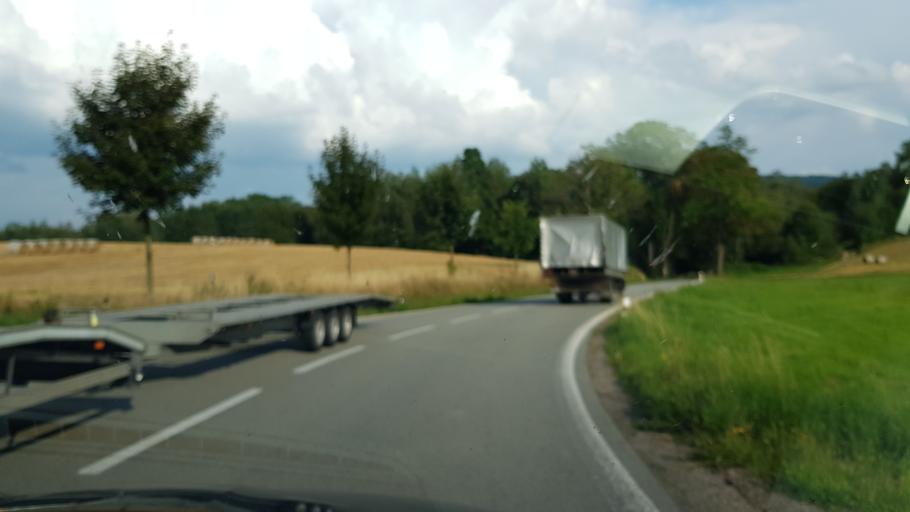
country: CZ
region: Pardubicky
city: Jablonne nad Orlici
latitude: 50.0969
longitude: 16.6171
